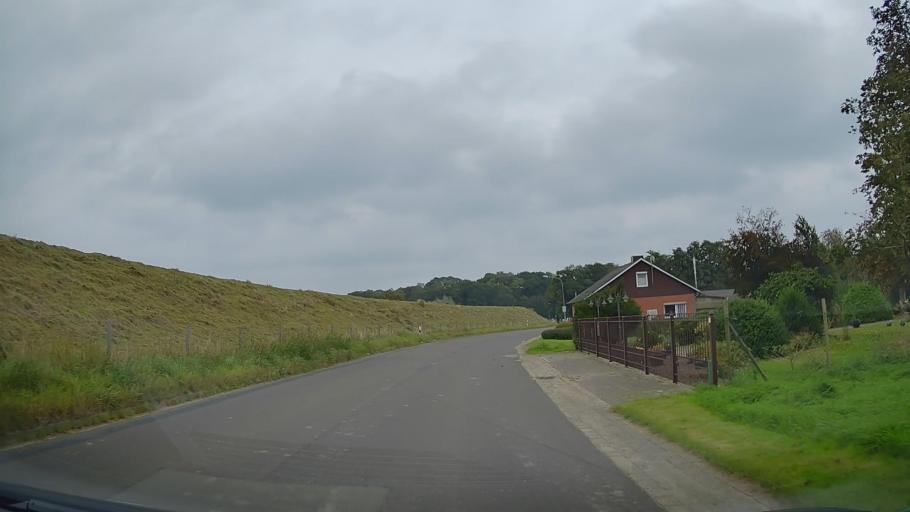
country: DE
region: Lower Saxony
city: Geversdorf
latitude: 53.8242
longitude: 9.0771
